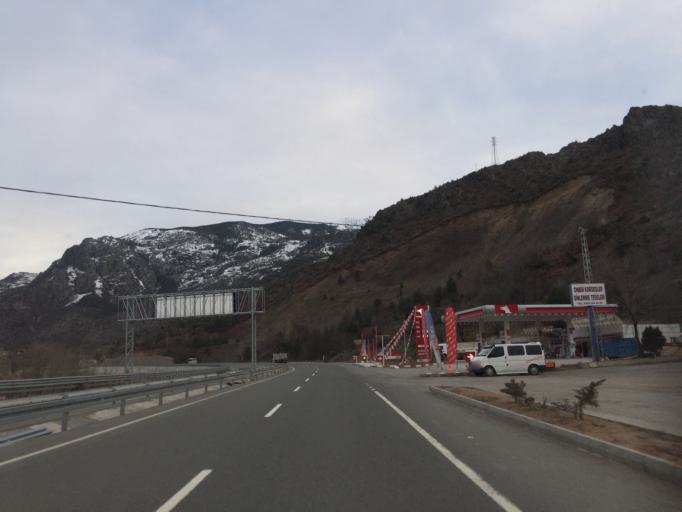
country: TR
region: Gumushane
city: Gumushkhane
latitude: 40.5068
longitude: 39.4227
